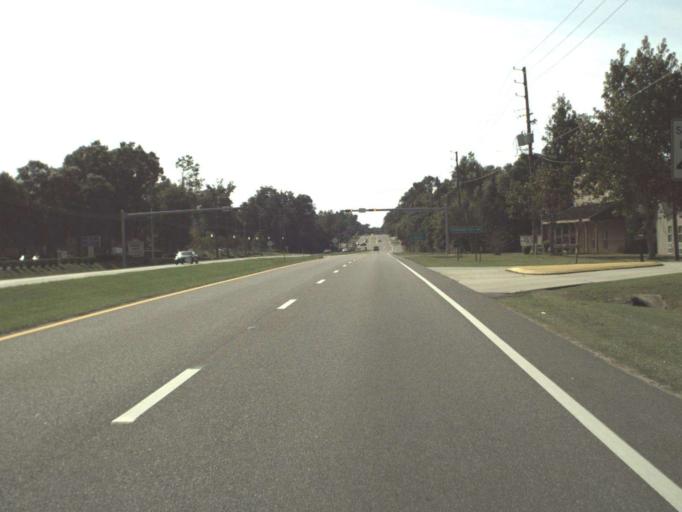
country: US
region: Florida
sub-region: Escambia County
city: Bellview
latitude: 30.4910
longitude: -87.3063
